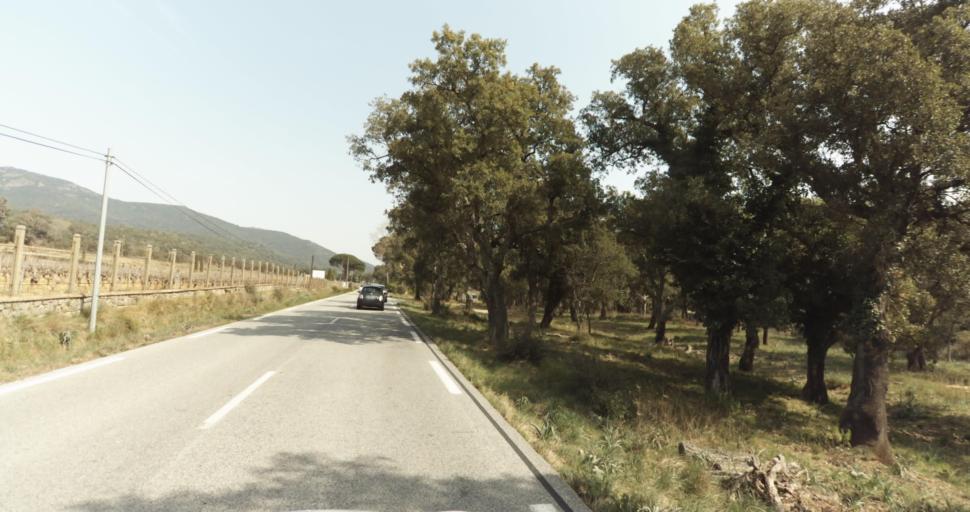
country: FR
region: Provence-Alpes-Cote d'Azur
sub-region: Departement du Var
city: Le Lavandou
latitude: 43.1964
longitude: 6.3856
